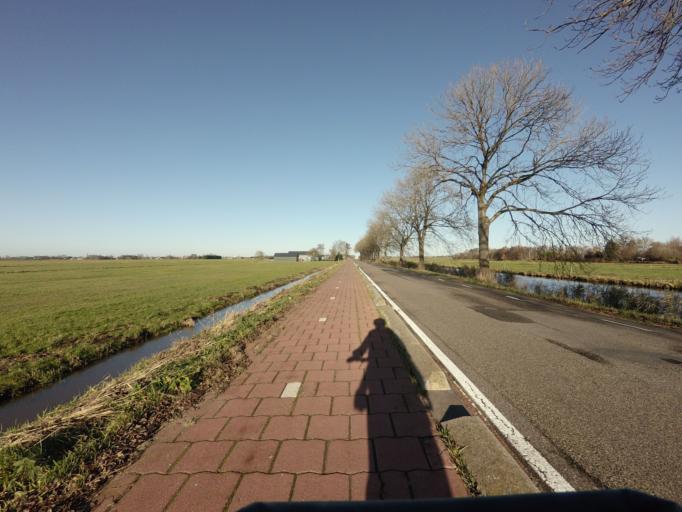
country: NL
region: Utrecht
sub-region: Gemeente De Ronde Venen
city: Mijdrecht
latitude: 52.2360
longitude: 4.9038
